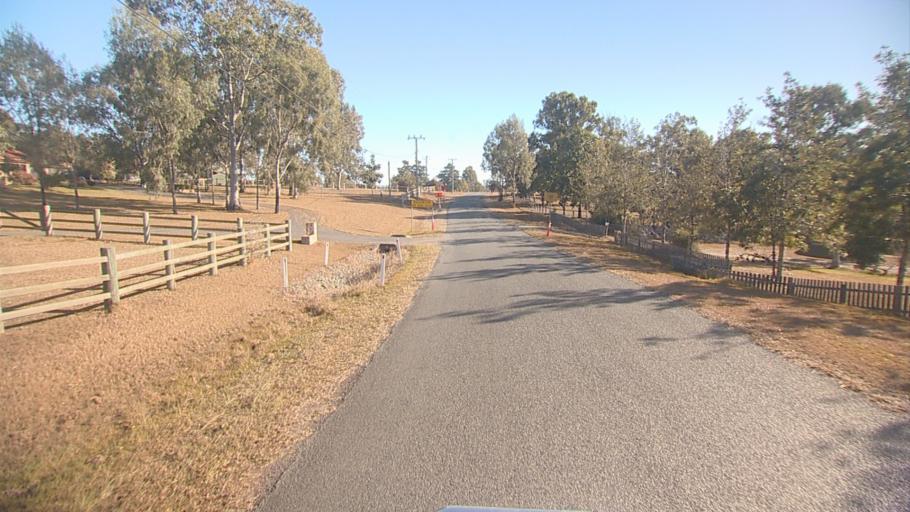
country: AU
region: Queensland
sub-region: Logan
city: Cedar Vale
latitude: -27.8332
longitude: 153.0058
